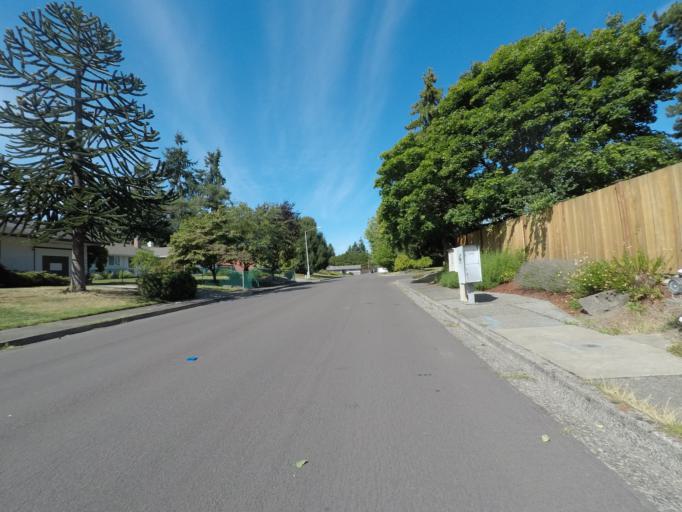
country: US
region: Washington
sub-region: King County
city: Inglewood-Finn Hill
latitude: 47.7309
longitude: -122.2304
